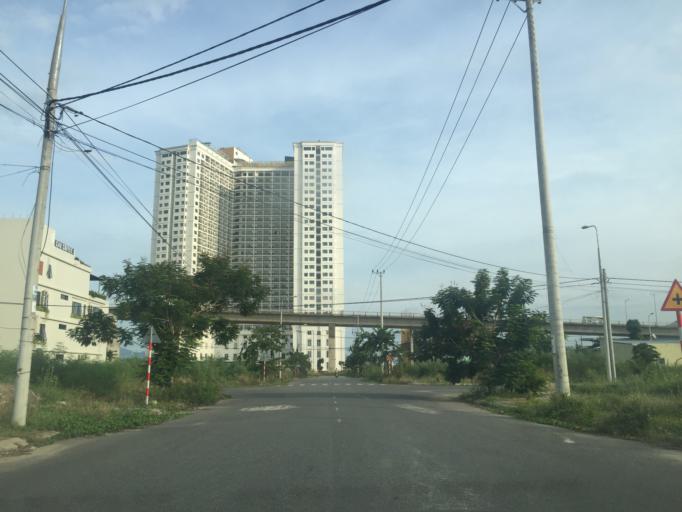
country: VN
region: Da Nang
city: Da Nang
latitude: 16.0960
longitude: 108.2261
